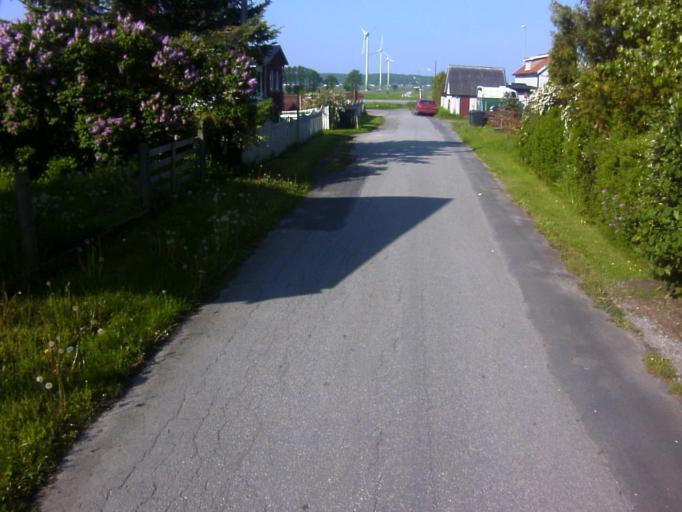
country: SE
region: Blekinge
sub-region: Solvesborgs Kommun
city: Soelvesborg
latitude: 56.0458
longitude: 14.6653
